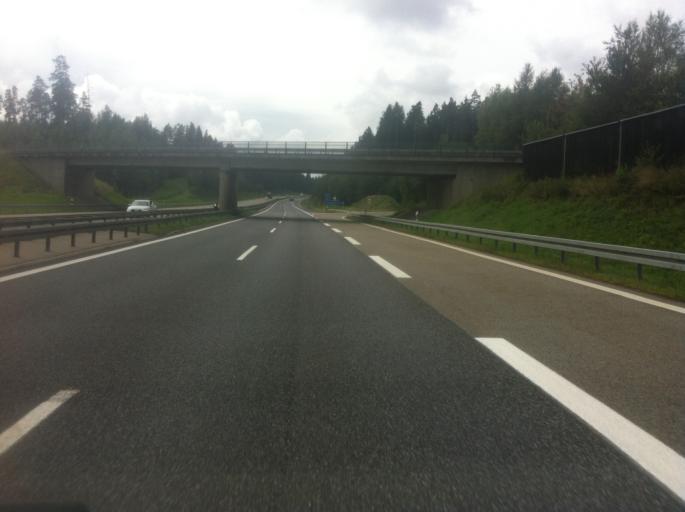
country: DE
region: Bavaria
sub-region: Upper Palatinate
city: Pleystein
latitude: 49.6199
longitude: 12.4172
